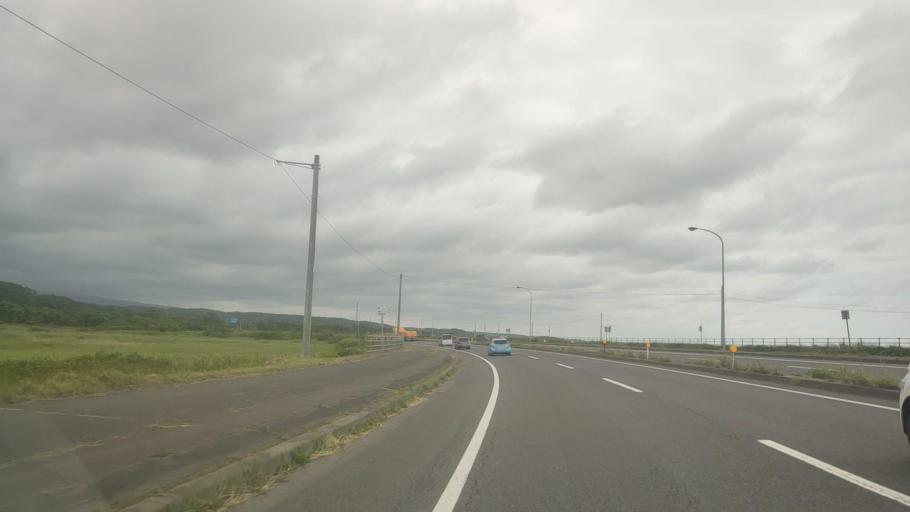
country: JP
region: Hokkaido
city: Shiraoi
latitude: 42.5577
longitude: 141.3793
